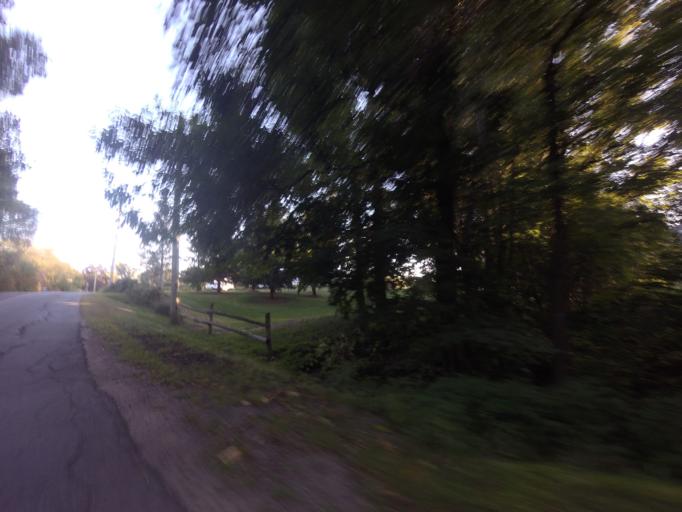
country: CA
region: Quebec
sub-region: Monteregie
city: Hudson
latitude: 45.4823
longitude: -74.2063
